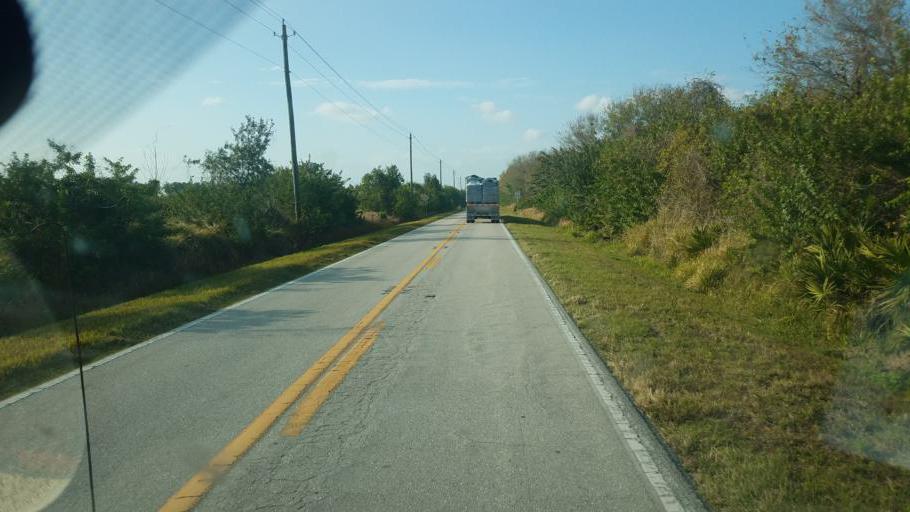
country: US
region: Florida
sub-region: Hardee County
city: Bowling Green
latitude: 27.7235
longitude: -81.9640
